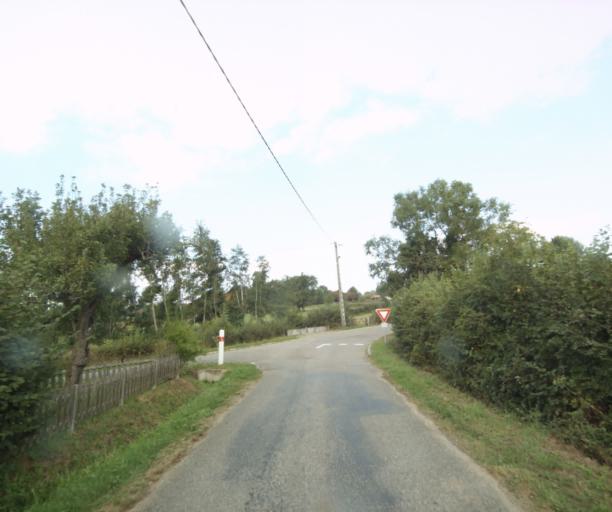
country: FR
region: Bourgogne
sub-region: Departement de Saone-et-Loire
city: Palinges
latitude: 46.5244
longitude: 4.2549
